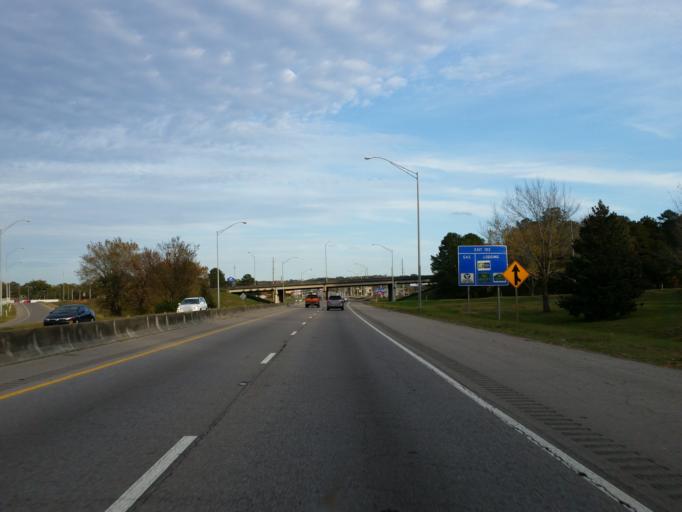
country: US
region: Mississippi
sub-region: Lauderdale County
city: Meridian
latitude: 32.3490
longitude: -88.7137
